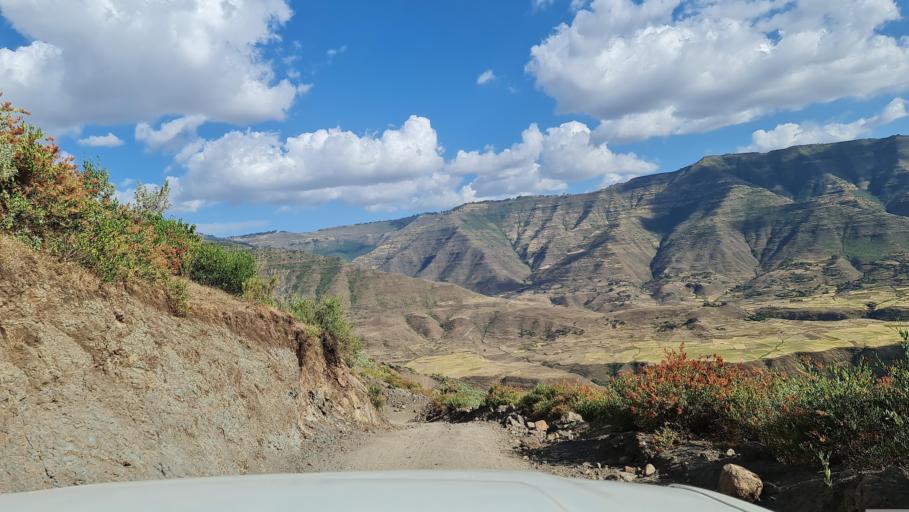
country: ET
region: Amhara
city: Debark'
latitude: 13.1205
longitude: 38.0192
